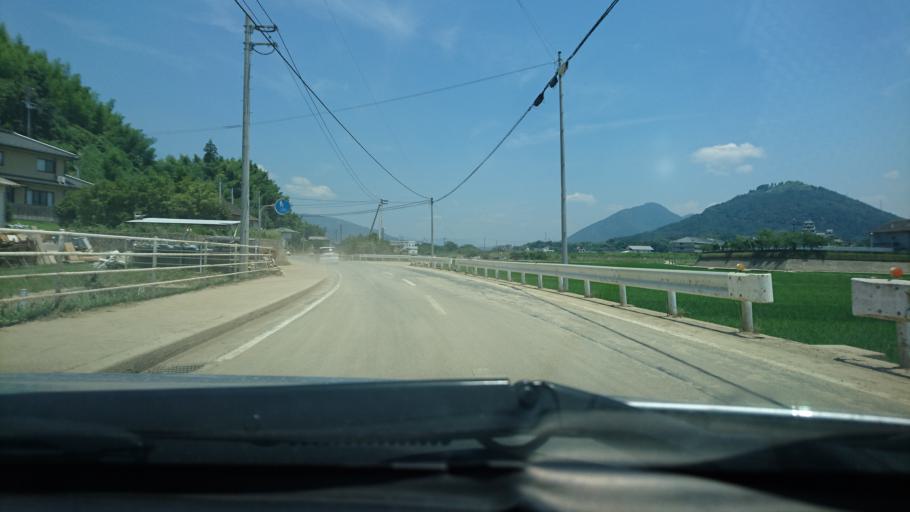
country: JP
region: Ehime
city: Ozu
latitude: 33.5100
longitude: 132.5332
